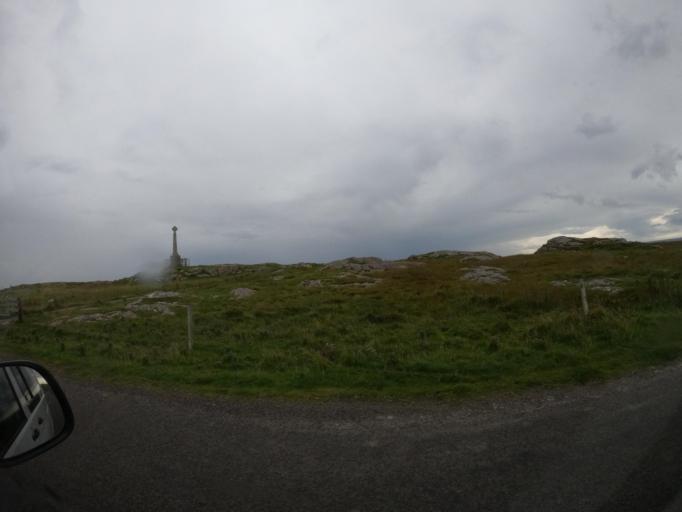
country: GB
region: Scotland
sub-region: Eilean Siar
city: Barra
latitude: 56.5062
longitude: -6.8015
